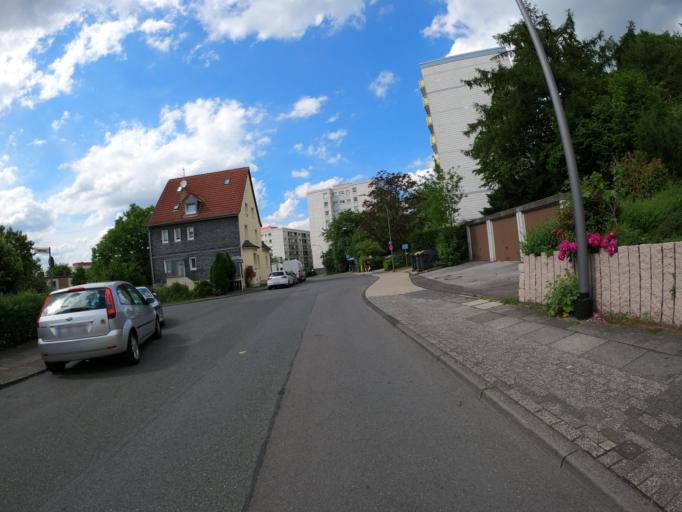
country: DE
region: North Rhine-Westphalia
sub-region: Regierungsbezirk Dusseldorf
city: Wuppertal
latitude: 51.2534
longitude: 7.1161
